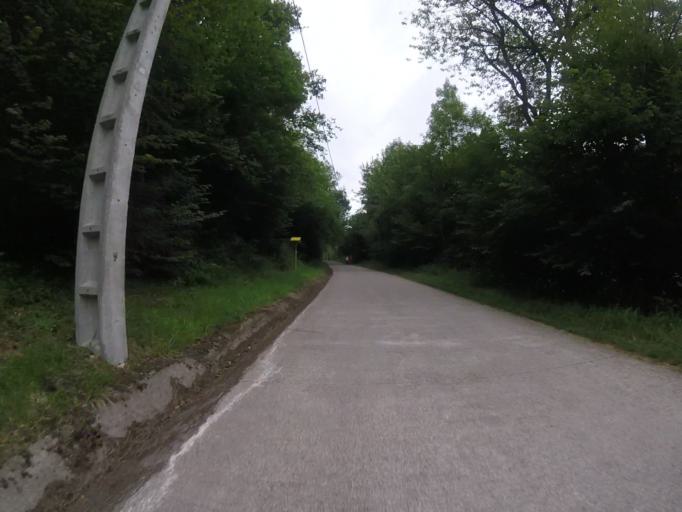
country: ES
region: Navarre
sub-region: Provincia de Navarra
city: Doneztebe
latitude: 43.1451
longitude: -1.6688
